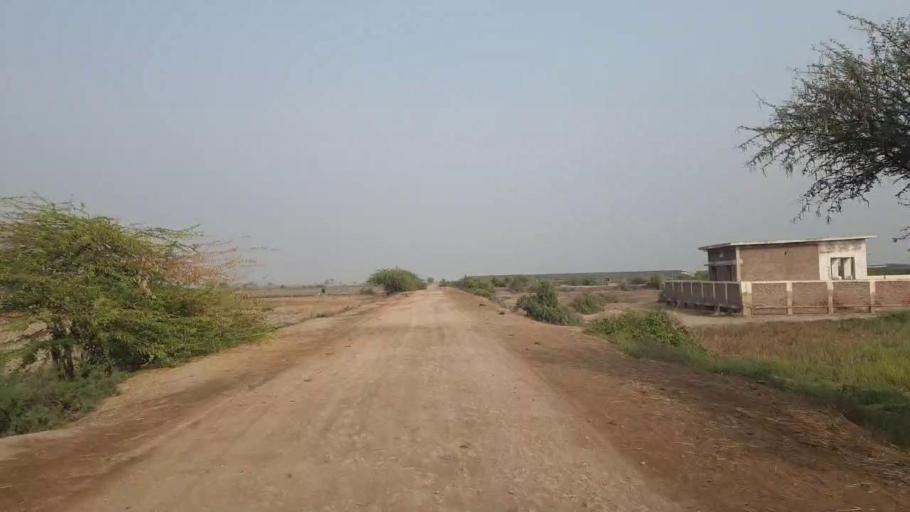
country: PK
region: Sindh
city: Mirpur Batoro
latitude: 24.5906
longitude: 68.4076
